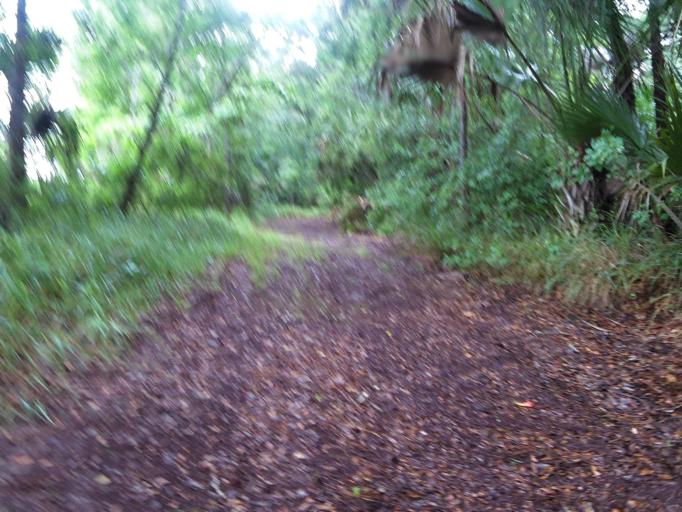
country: US
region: Florida
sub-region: Putnam County
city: Palatka
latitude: 29.6831
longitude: -81.7446
